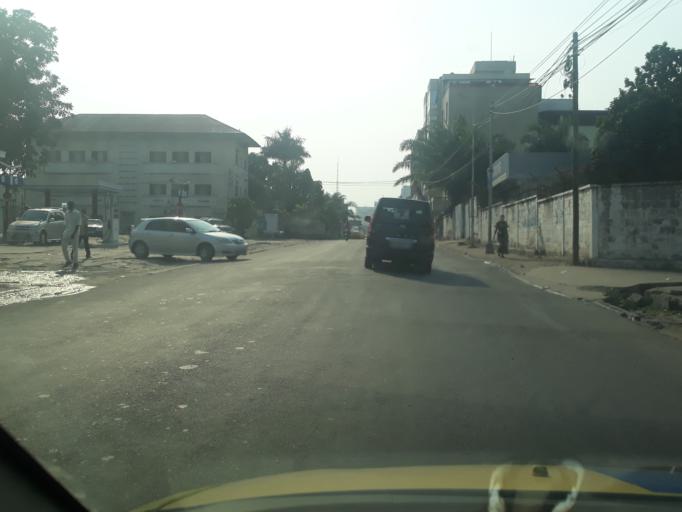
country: CD
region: Kinshasa
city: Kinshasa
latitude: -4.3065
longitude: 15.3243
